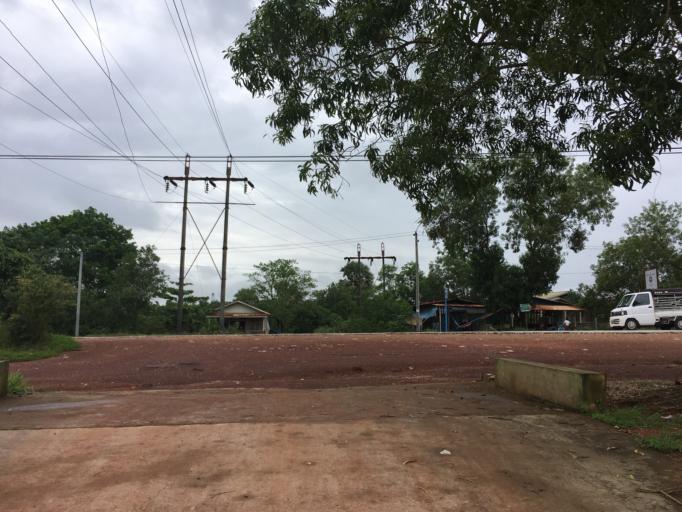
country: MM
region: Mon
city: Mawlamyine
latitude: 16.4789
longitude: 97.6741
